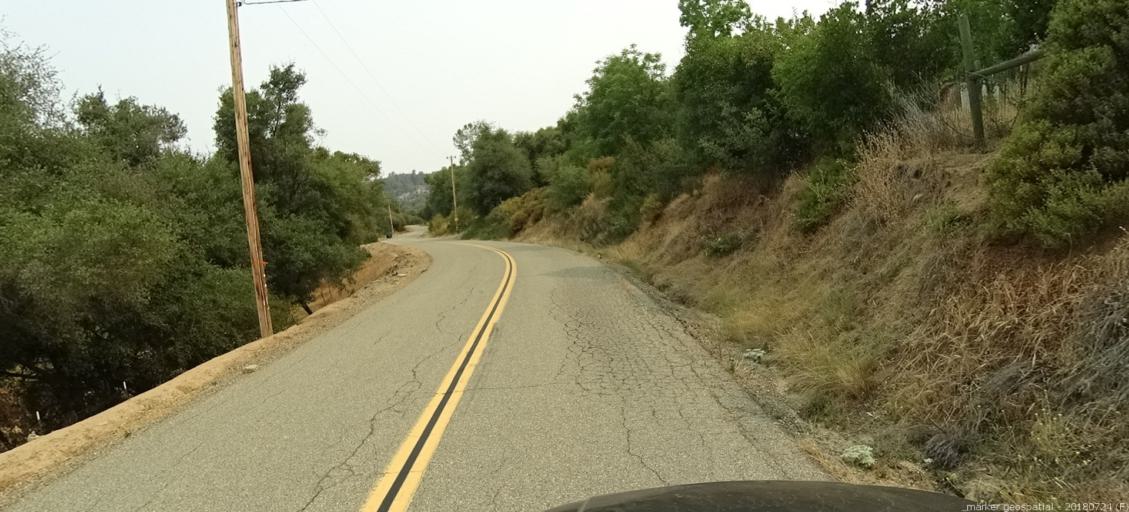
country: US
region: California
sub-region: Madera County
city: Oakhurst
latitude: 37.3393
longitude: -119.6069
